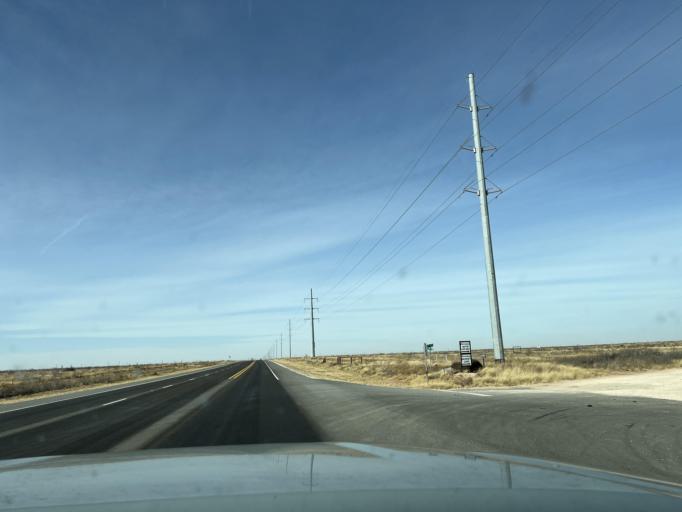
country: US
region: Texas
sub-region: Andrews County
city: Andrews
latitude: 32.3412
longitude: -102.6916
